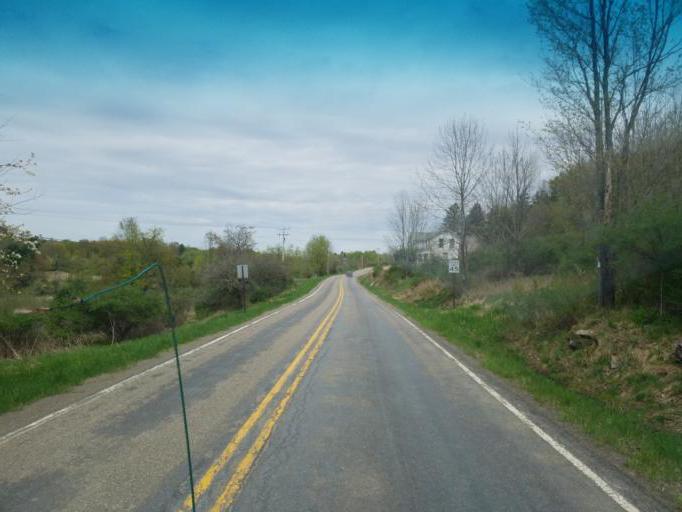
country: US
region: Pennsylvania
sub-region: Tioga County
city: Wellsboro
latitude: 41.6951
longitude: -77.4294
